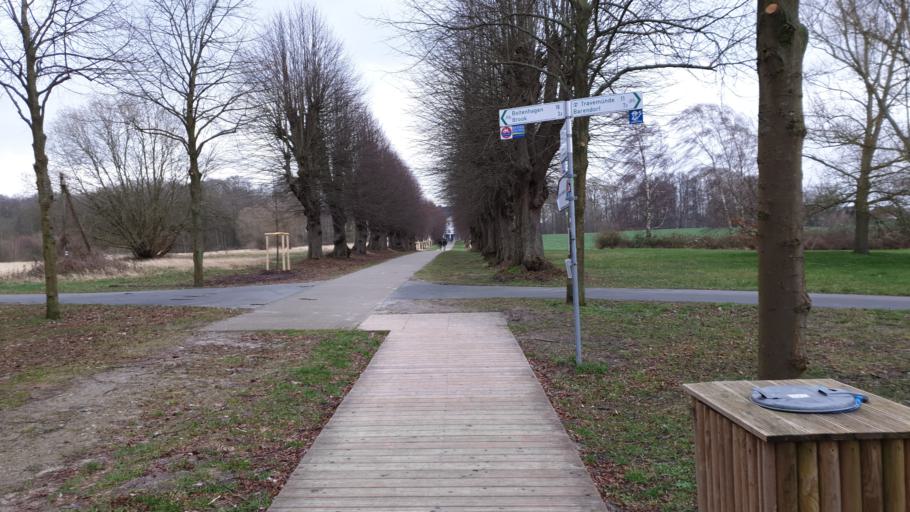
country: DE
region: Mecklenburg-Vorpommern
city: Kalkhorst
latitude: 53.9939
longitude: 11.0064
